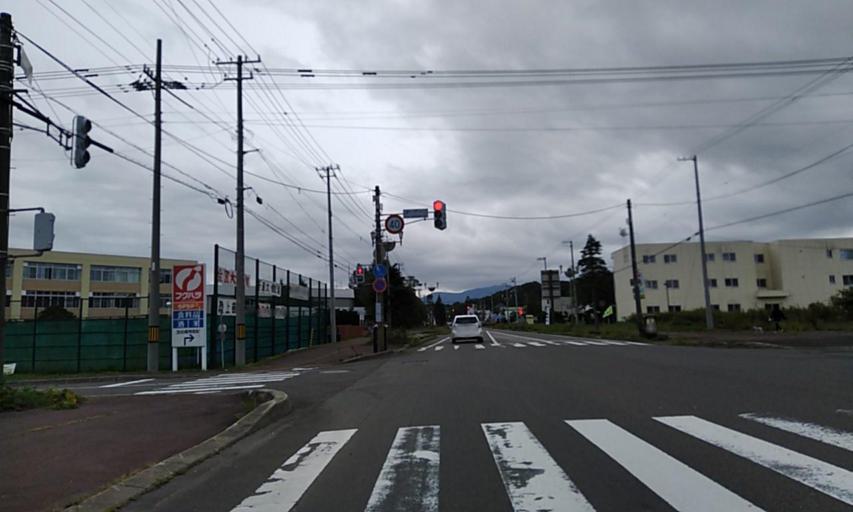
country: JP
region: Hokkaido
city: Obihiro
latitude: 42.2980
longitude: 143.3145
